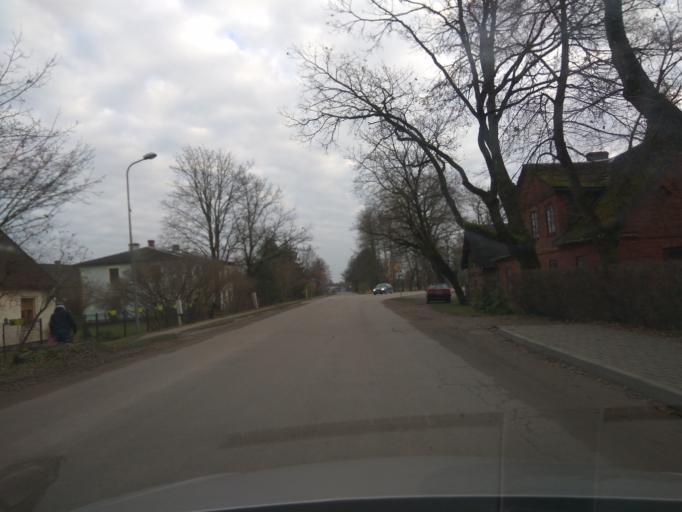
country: LV
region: Kuldigas Rajons
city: Kuldiga
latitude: 56.9619
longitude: 21.9840
